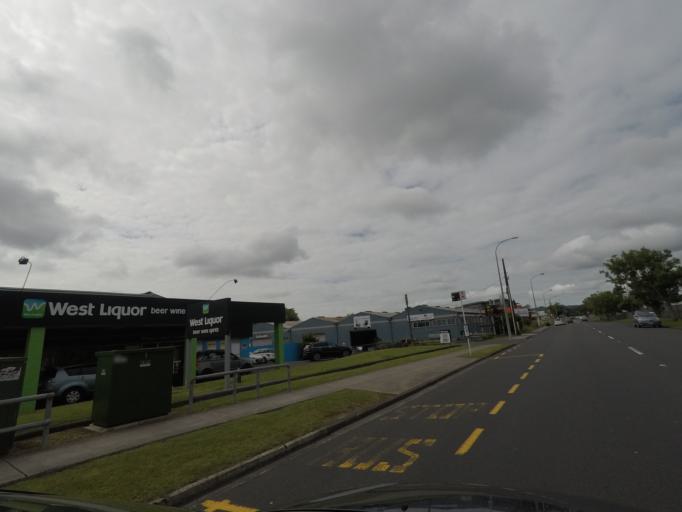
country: NZ
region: Auckland
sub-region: Auckland
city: Waitakere
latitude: -36.8888
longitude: 174.6317
